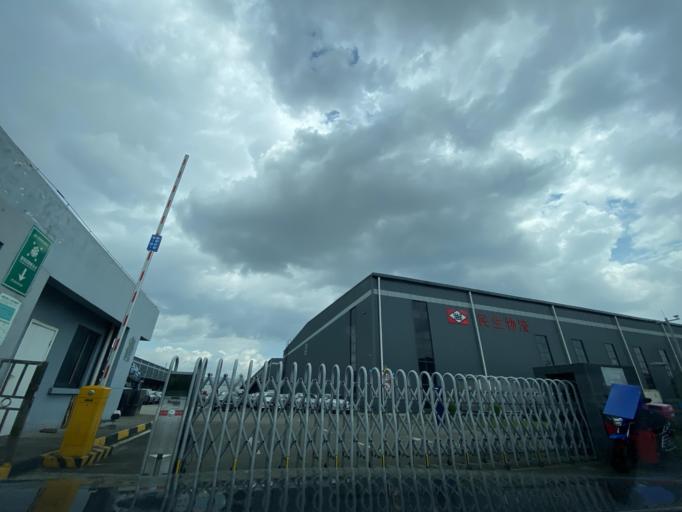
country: CN
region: Sichuan
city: Longquan
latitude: 30.5325
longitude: 104.1958
